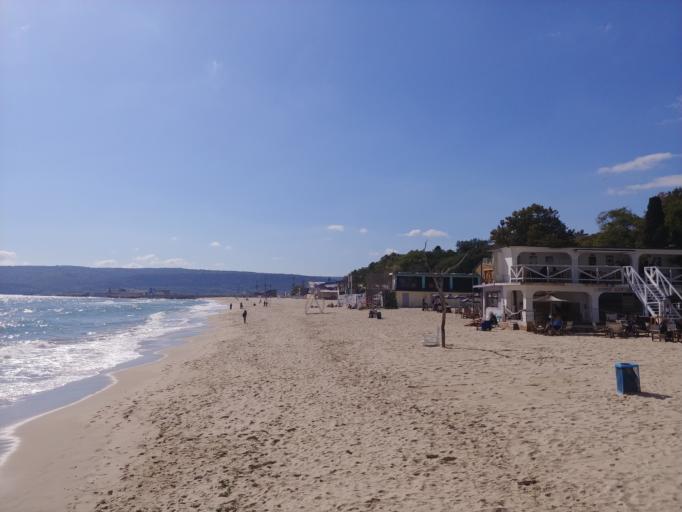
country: BG
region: Varna
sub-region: Obshtina Varna
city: Varna
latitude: 43.2024
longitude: 27.9245
